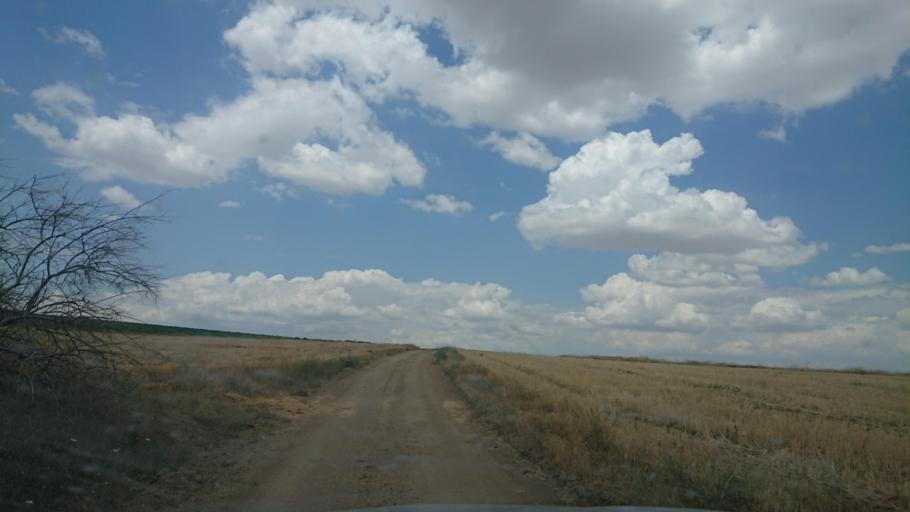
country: TR
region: Aksaray
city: Agacoren
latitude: 38.8953
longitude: 33.8829
